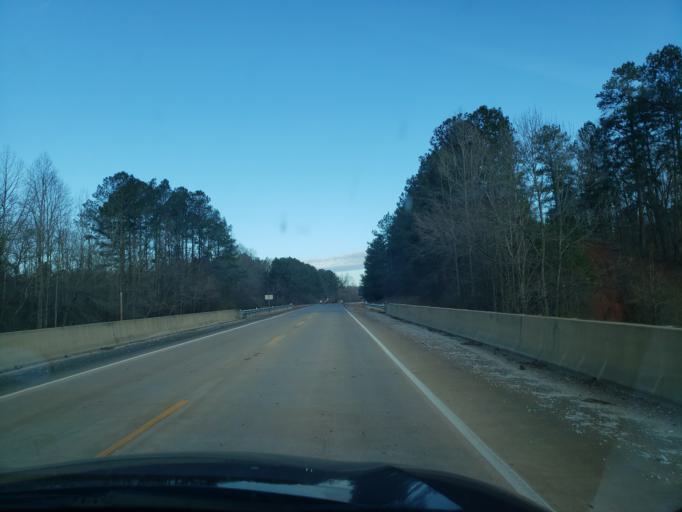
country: US
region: Alabama
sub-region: Cleburne County
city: Heflin
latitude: 33.5096
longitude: -85.6249
